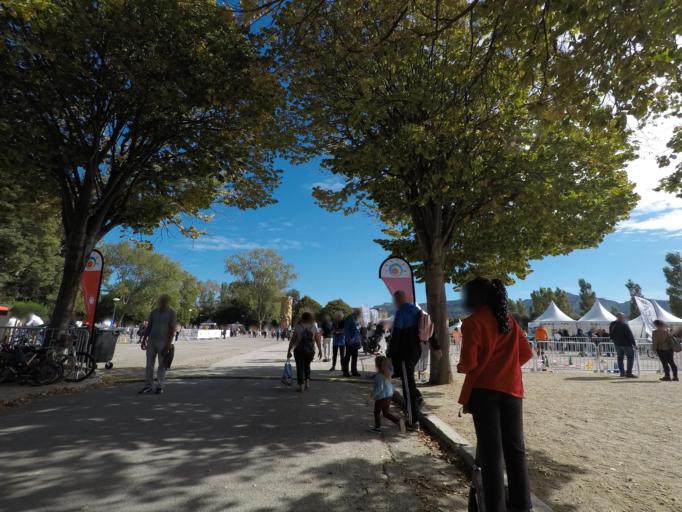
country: FR
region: Provence-Alpes-Cote d'Azur
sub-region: Departement des Bouches-du-Rhone
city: Marseille 08
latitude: 43.2603
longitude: 5.3806
